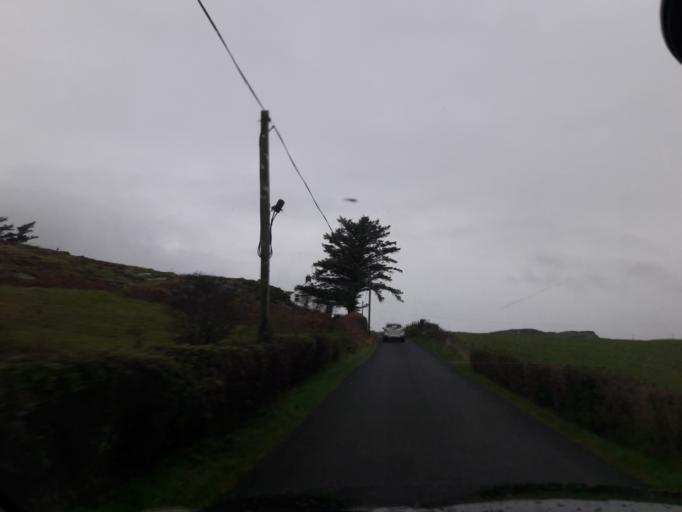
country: IE
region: Ulster
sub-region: County Donegal
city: Buncrana
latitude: 55.2427
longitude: -7.6226
